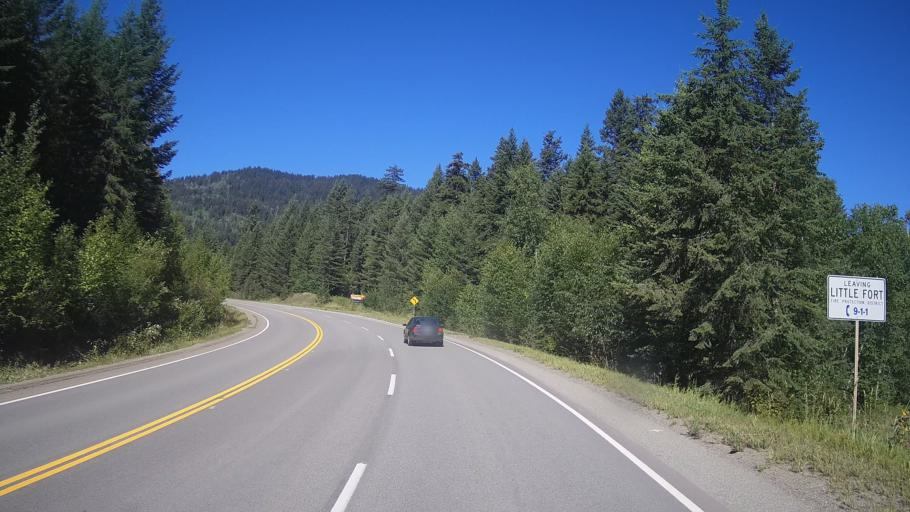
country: CA
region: British Columbia
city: Kamloops
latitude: 51.4668
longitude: -120.2360
